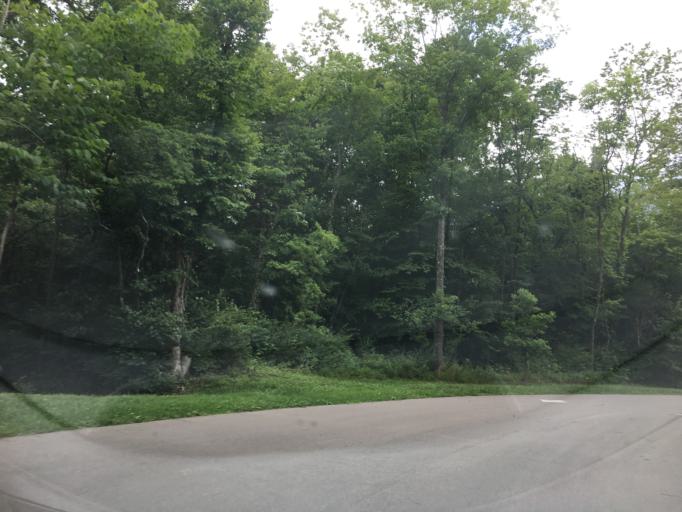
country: US
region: Tennessee
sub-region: Davidson County
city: Belle Meade
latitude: 36.0629
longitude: -86.9053
